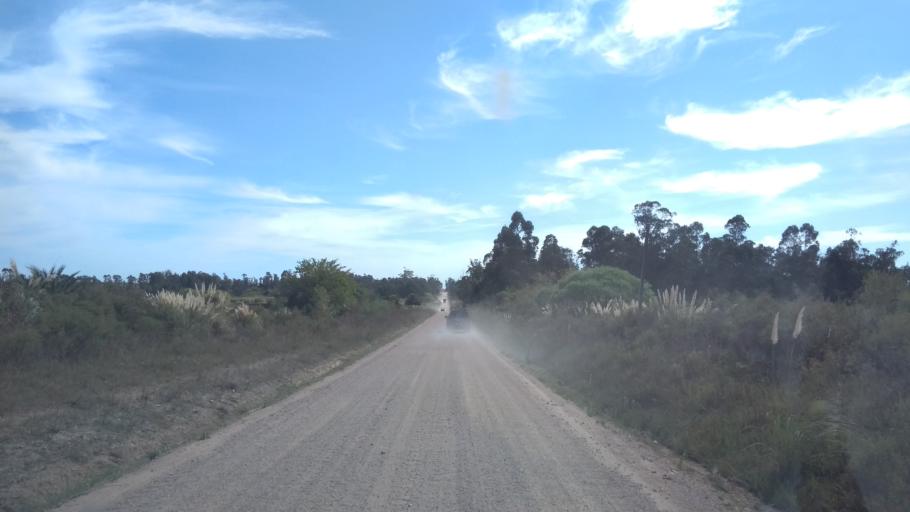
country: UY
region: Canelones
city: Joaquin Suarez
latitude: -34.7106
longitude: -56.0241
